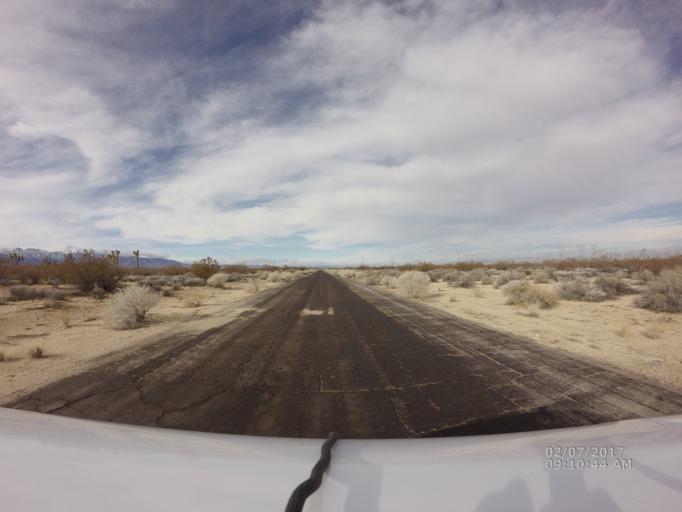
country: US
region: California
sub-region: San Bernardino County
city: Pinon Hills
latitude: 34.5276
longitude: -117.7275
